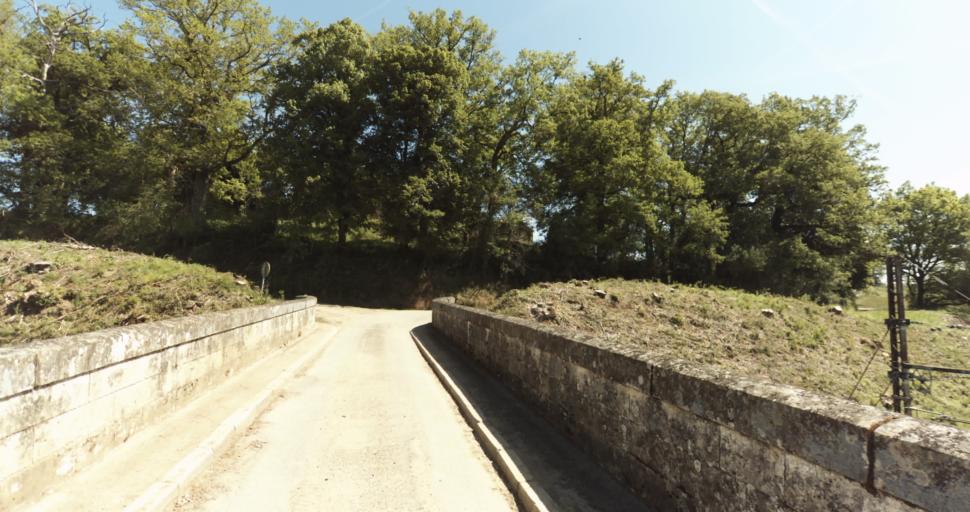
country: FR
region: Limousin
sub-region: Departement de la Haute-Vienne
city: Le Vigen
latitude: 45.7517
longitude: 1.2958
